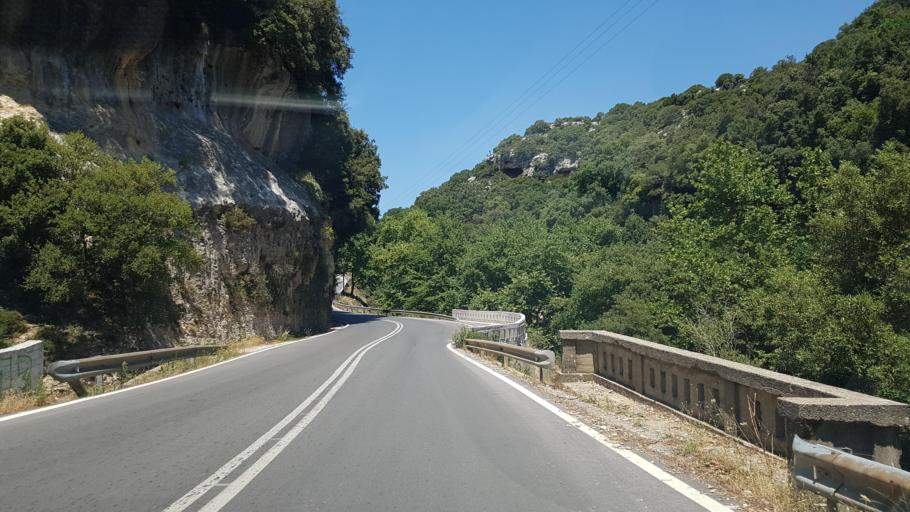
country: GR
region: Crete
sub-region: Nomos Rethymnis
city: Agia Foteini
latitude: 35.3106
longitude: 24.6269
